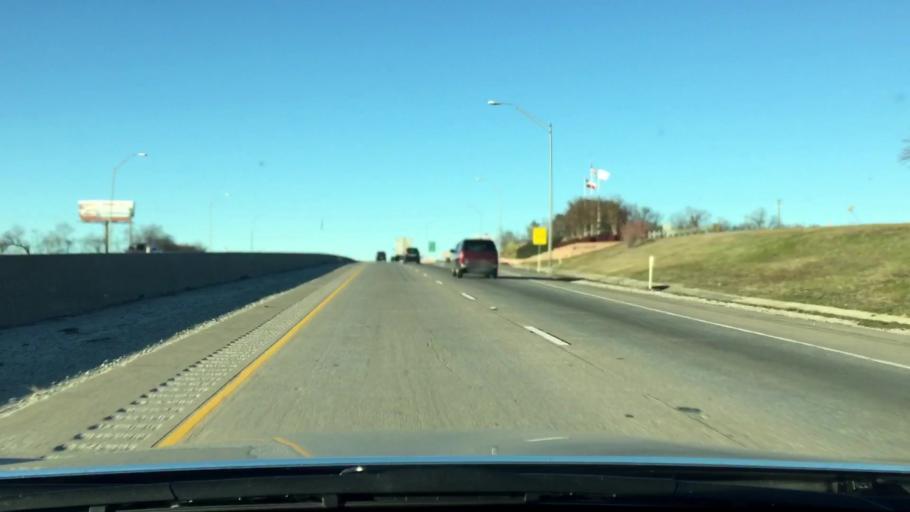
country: US
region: Texas
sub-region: Denton County
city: Sanger
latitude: 33.3446
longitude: -97.1816
